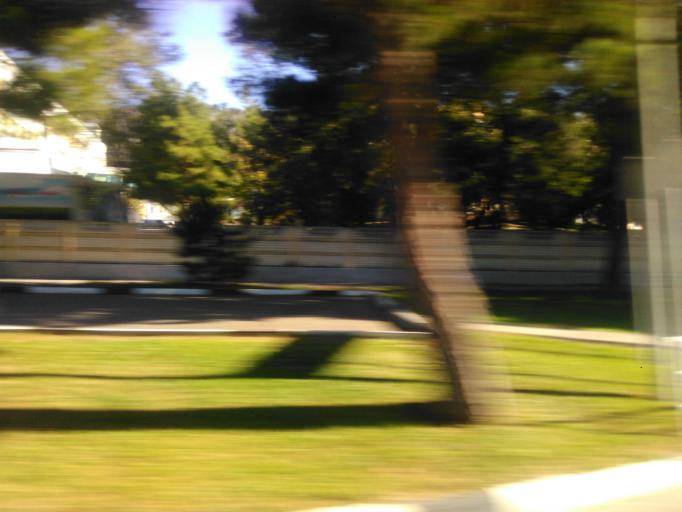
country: RU
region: Krasnodarskiy
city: Gelendzhik
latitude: 44.5807
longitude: 38.0657
